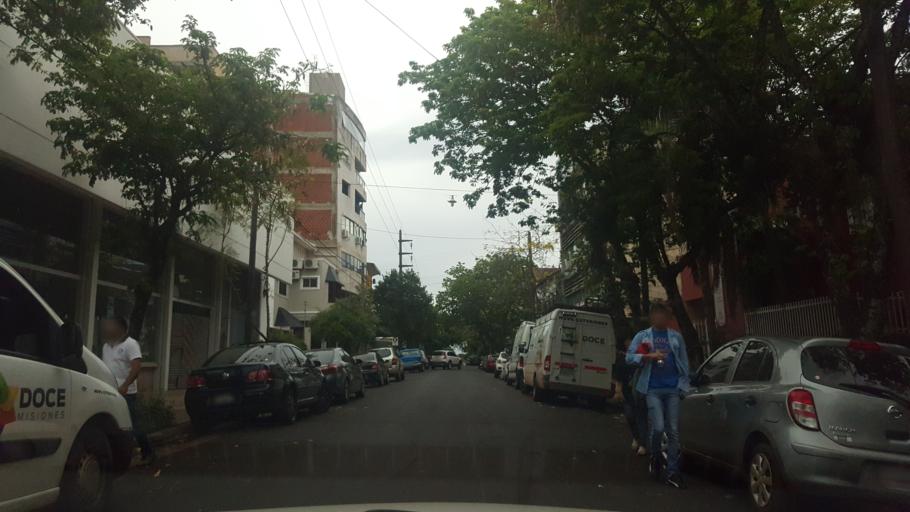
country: AR
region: Misiones
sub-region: Departamento de Capital
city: Posadas
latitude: -27.3683
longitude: -55.8885
